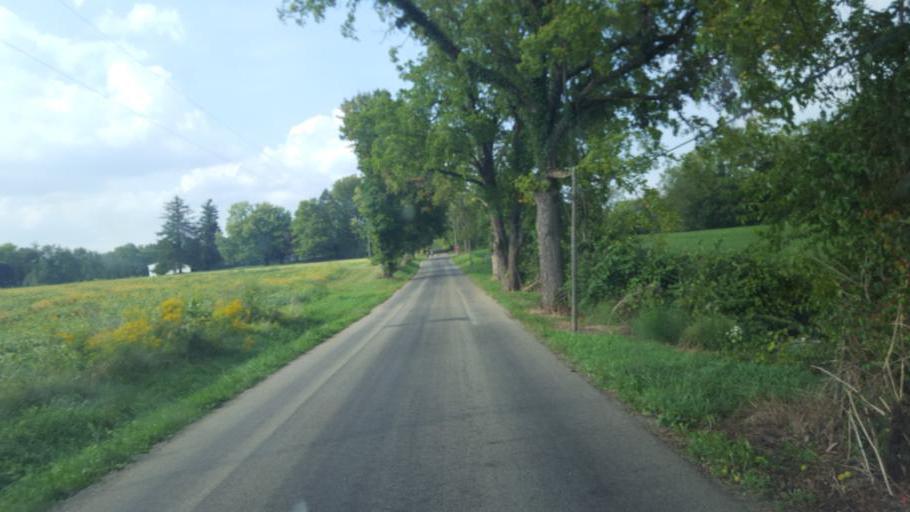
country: US
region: Ohio
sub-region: Knox County
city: Gambier
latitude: 40.3694
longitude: -82.4382
